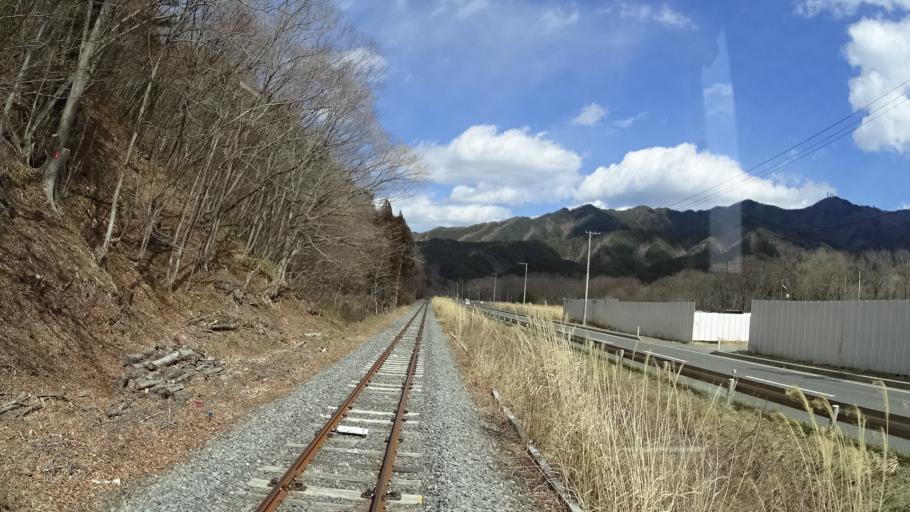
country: JP
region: Iwate
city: Yamada
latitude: 39.5433
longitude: 141.9327
